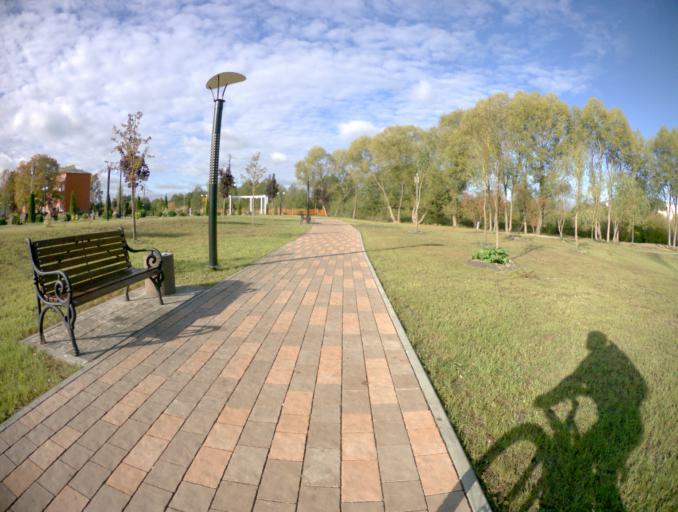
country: RU
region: Moskovskaya
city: Roshal'
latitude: 55.6613
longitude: 39.8654
